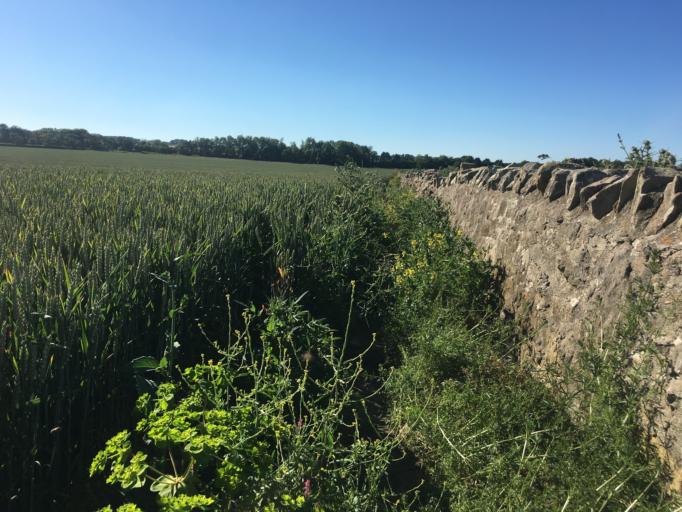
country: GB
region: England
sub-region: Northumberland
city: Beadnell
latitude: 55.5634
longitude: -1.6467
